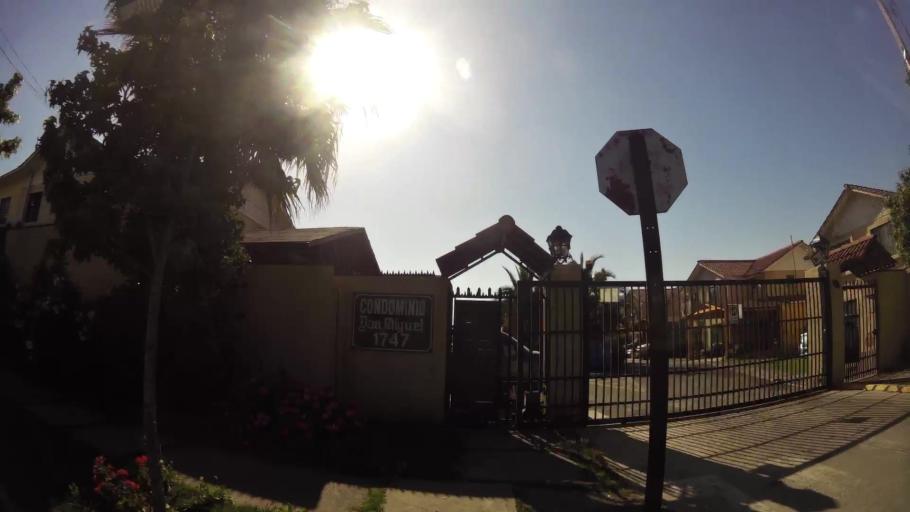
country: CL
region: Santiago Metropolitan
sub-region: Provincia de Maipo
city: San Bernardo
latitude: -33.6152
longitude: -70.6912
